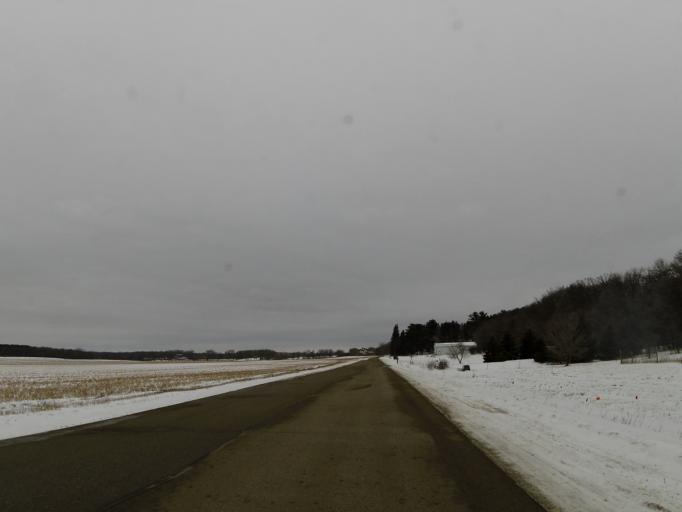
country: US
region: Minnesota
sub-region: Washington County
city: Stillwater
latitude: 45.0612
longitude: -92.7751
